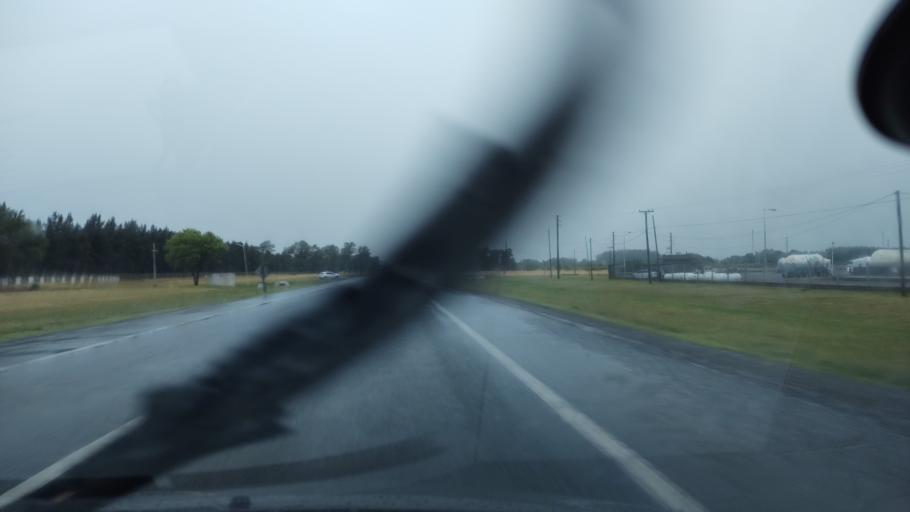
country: AR
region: Buenos Aires
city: Canuelas
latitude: -35.0566
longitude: -58.7908
